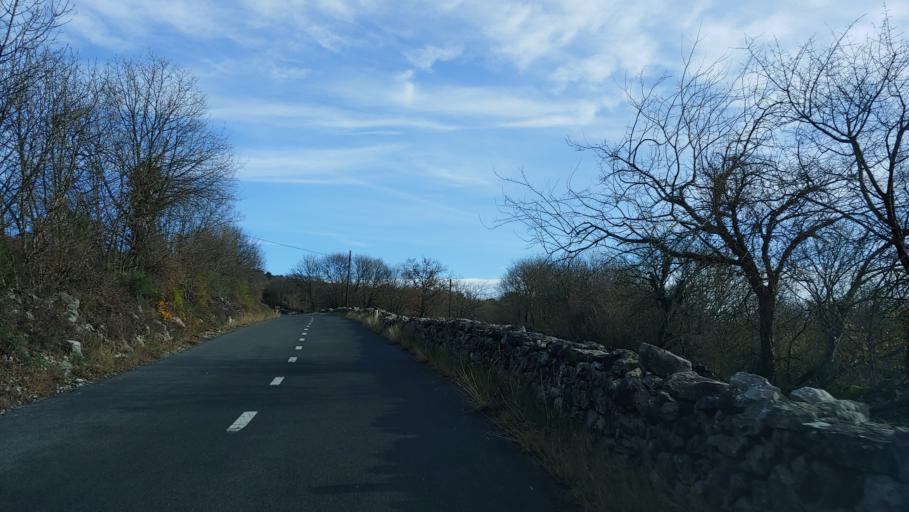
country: SI
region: Komen
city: Komen
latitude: 45.8100
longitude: 13.6889
